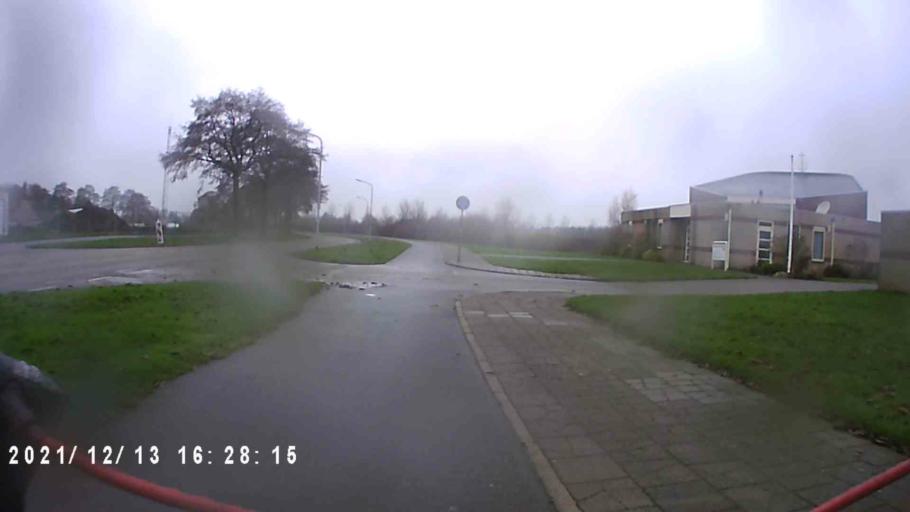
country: NL
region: Groningen
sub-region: Gemeente Appingedam
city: Appingedam
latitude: 53.3261
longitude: 6.8871
